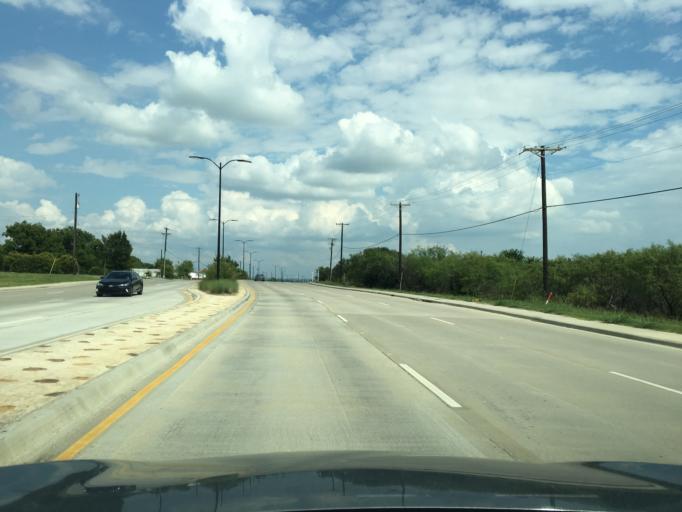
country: US
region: Texas
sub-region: Denton County
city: Oak Point
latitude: 33.1661
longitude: -96.9716
